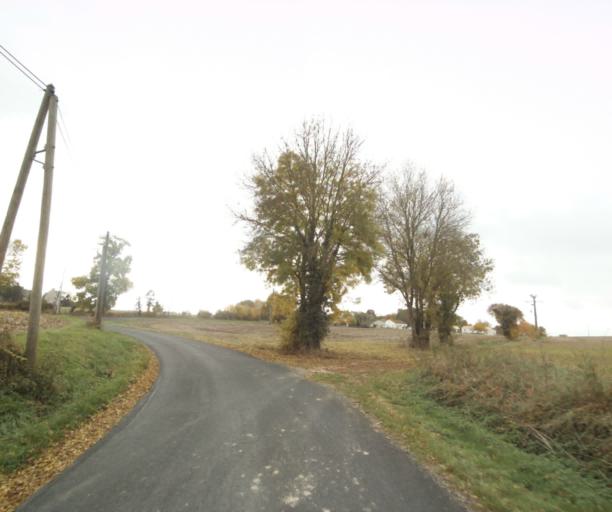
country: FR
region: Poitou-Charentes
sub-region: Departement de la Charente-Maritime
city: Saint-Georges-des-Coteaux
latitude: 45.7799
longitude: -0.6793
